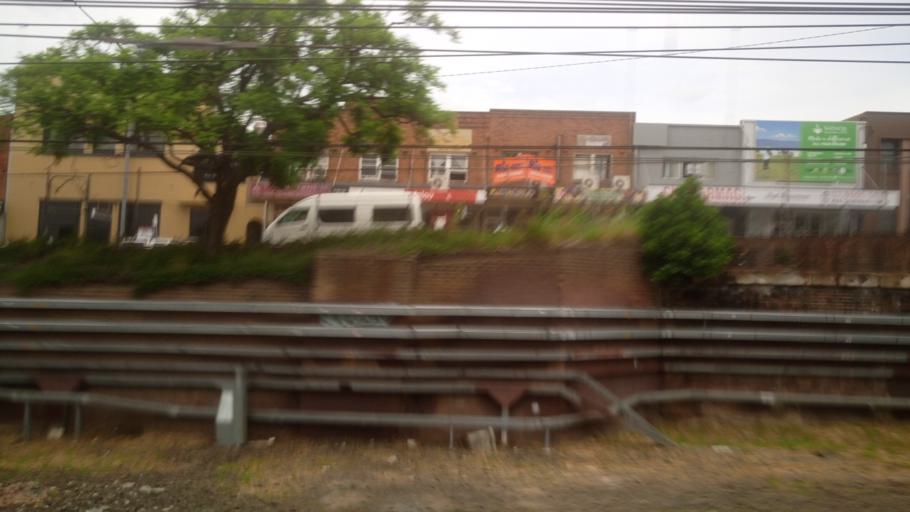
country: AU
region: New South Wales
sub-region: Parramatta
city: Granville
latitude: -33.8319
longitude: 151.0105
